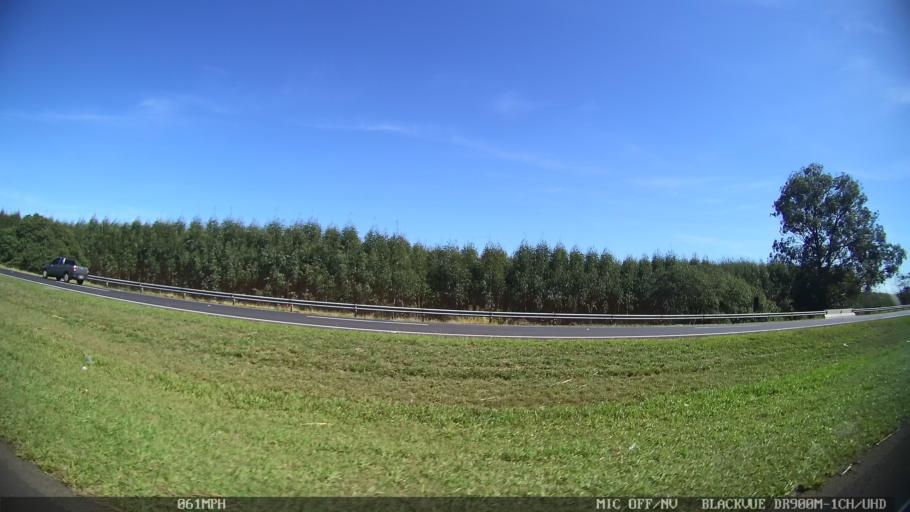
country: BR
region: Sao Paulo
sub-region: Sao Simao
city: Sao Simao
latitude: -21.5622
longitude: -47.6343
